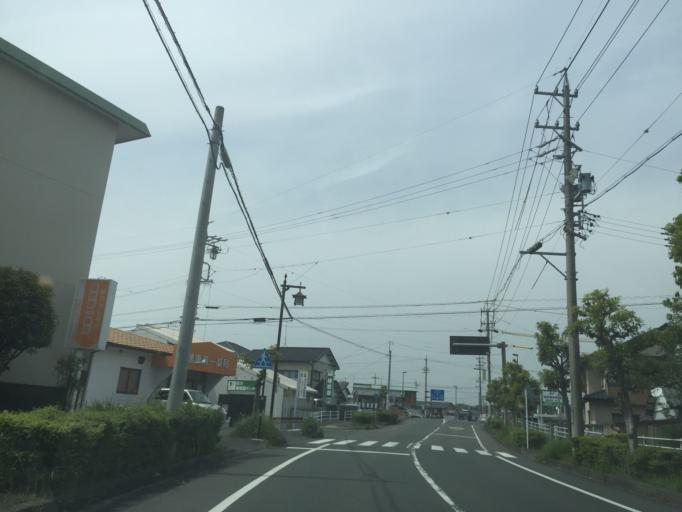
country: JP
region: Shizuoka
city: Kakegawa
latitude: 34.7750
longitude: 138.0025
